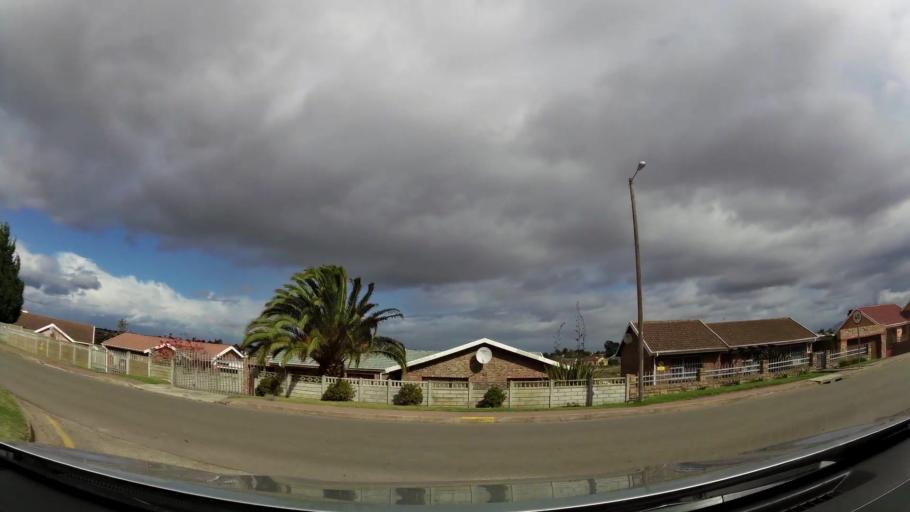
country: ZA
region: Western Cape
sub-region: Eden District Municipality
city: George
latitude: -33.9726
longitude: 22.4874
